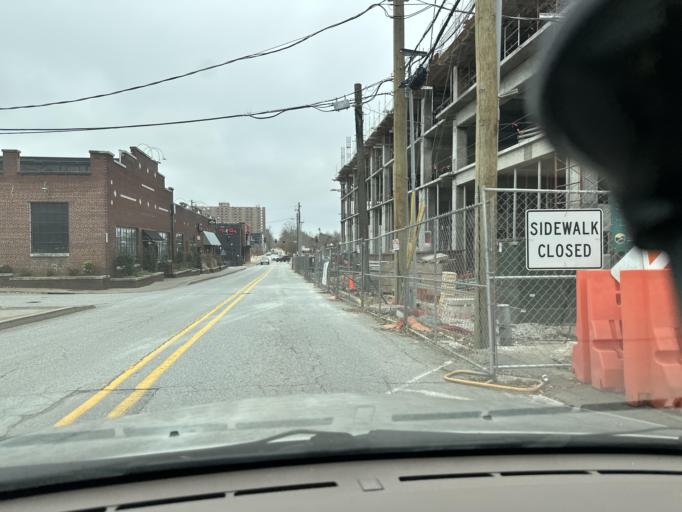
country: US
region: Arkansas
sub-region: Washington County
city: Fayetteville
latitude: 36.0677
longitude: -94.1654
